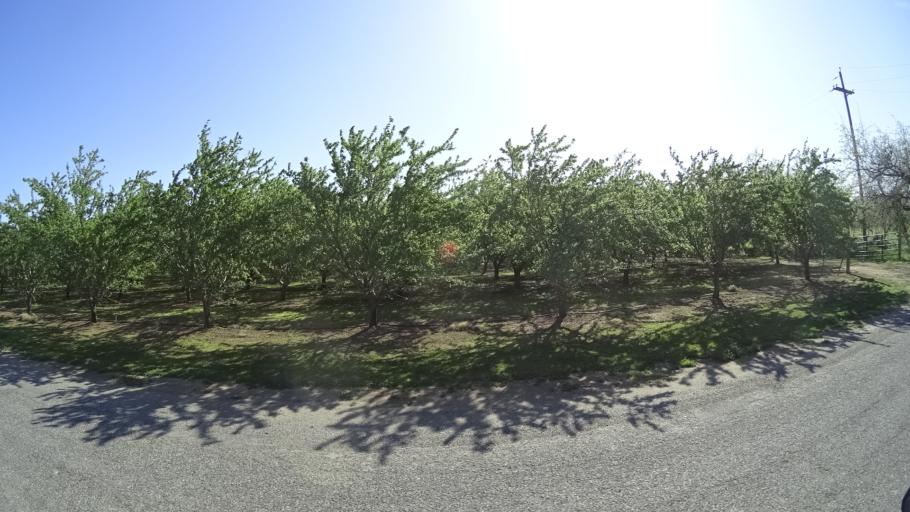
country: US
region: California
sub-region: Glenn County
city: Hamilton City
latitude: 39.7943
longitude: -122.0571
